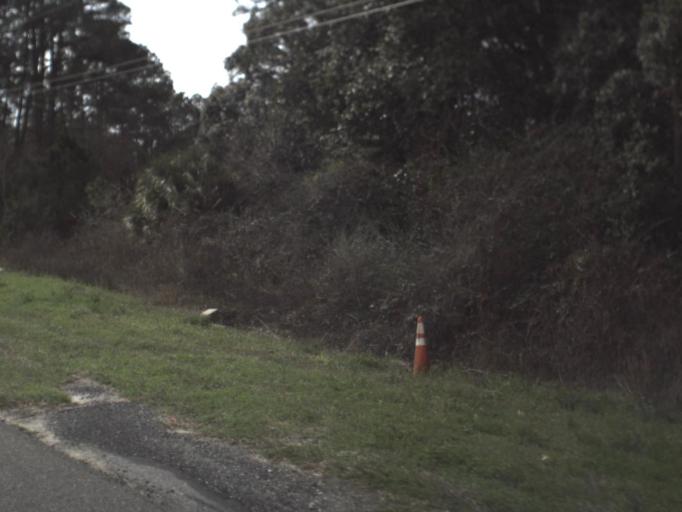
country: US
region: Florida
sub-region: Bay County
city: Hiland Park
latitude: 30.2056
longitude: -85.6183
